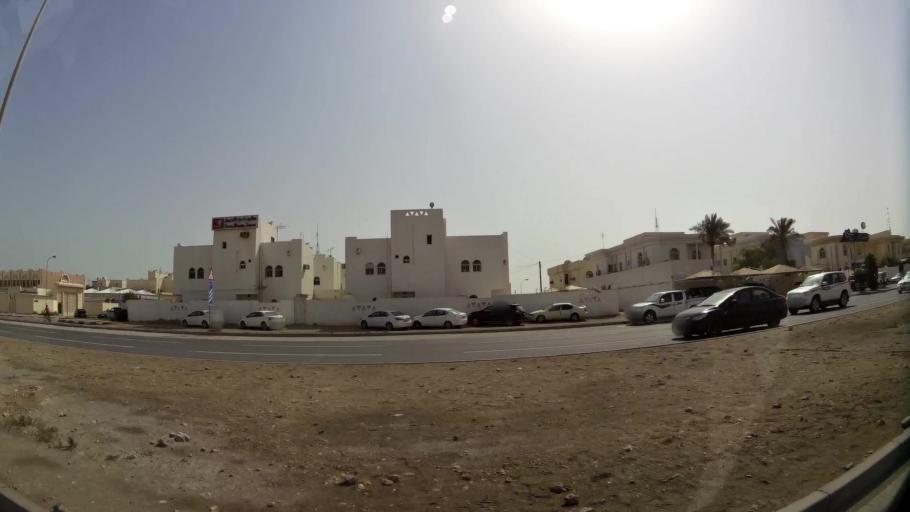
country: QA
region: Baladiyat ad Dawhah
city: Doha
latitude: 25.2429
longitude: 51.5242
